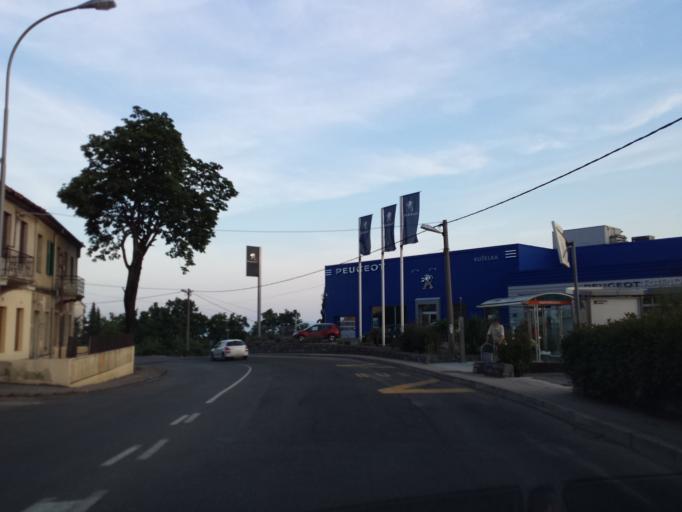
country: HR
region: Primorsko-Goranska
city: Rubesi
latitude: 45.3532
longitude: 14.3638
